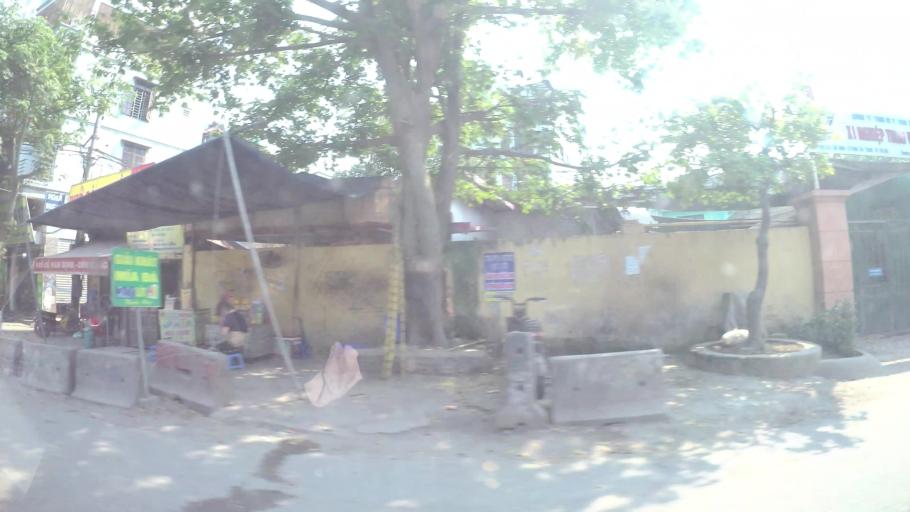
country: VN
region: Ha Noi
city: Ha Dong
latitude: 20.9590
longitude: 105.8043
